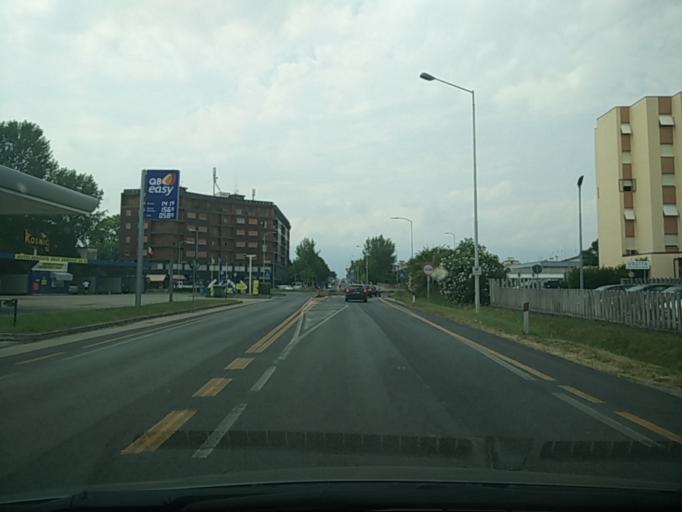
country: IT
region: Friuli Venezia Giulia
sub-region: Provincia di Pordenone
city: Pordenone
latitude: 45.9643
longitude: 12.6733
